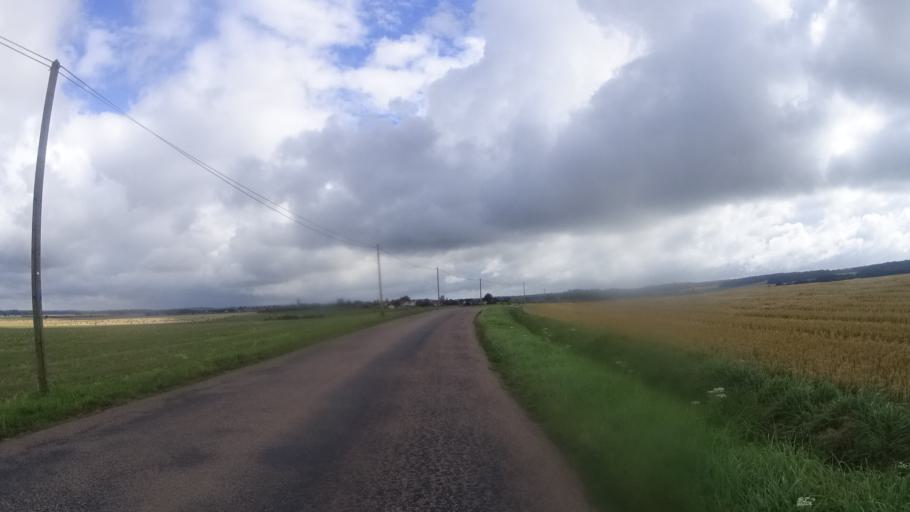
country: FR
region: Champagne-Ardenne
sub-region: Departement de l'Aube
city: Brienne-le-Chateau
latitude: 48.3649
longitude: 4.6158
